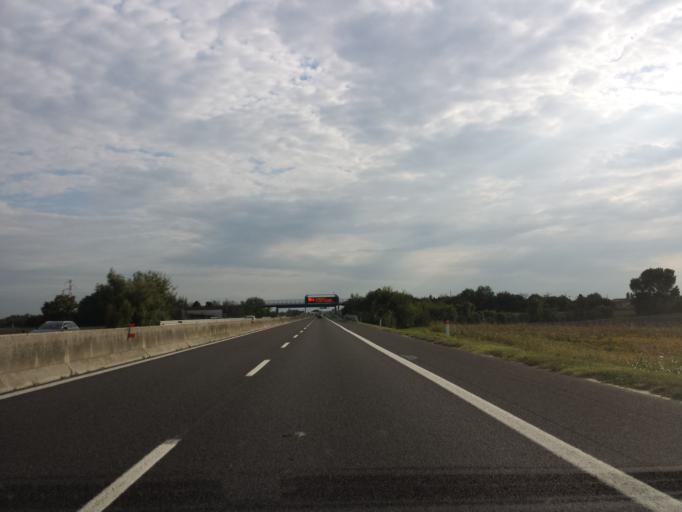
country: IT
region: Veneto
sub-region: Provincia di Padova
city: Stanghella
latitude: 45.1311
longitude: 11.7741
